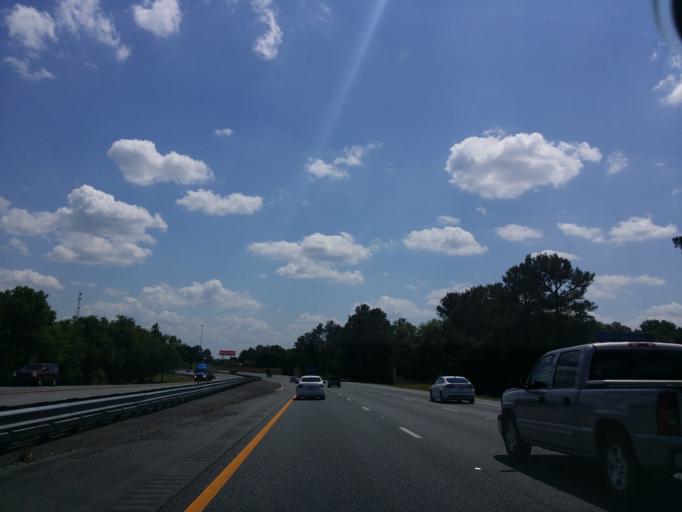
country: US
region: Florida
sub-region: Alachua County
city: High Springs
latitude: 30.0057
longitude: -82.6040
